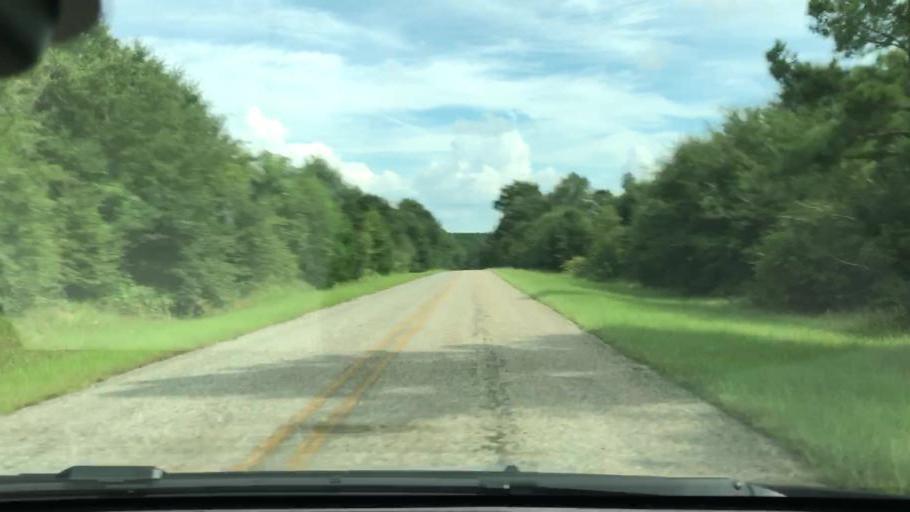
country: US
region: Georgia
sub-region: Early County
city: Blakely
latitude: 31.5065
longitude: -84.9479
